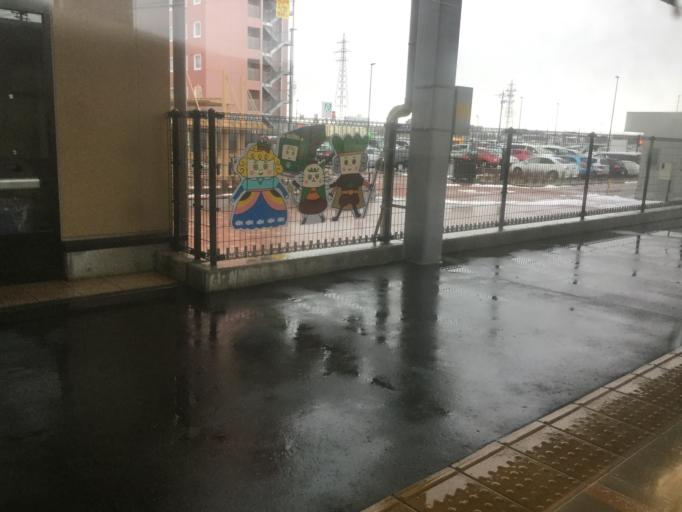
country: JP
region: Toyama
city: Takaoka
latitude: 36.7267
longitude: 137.0103
